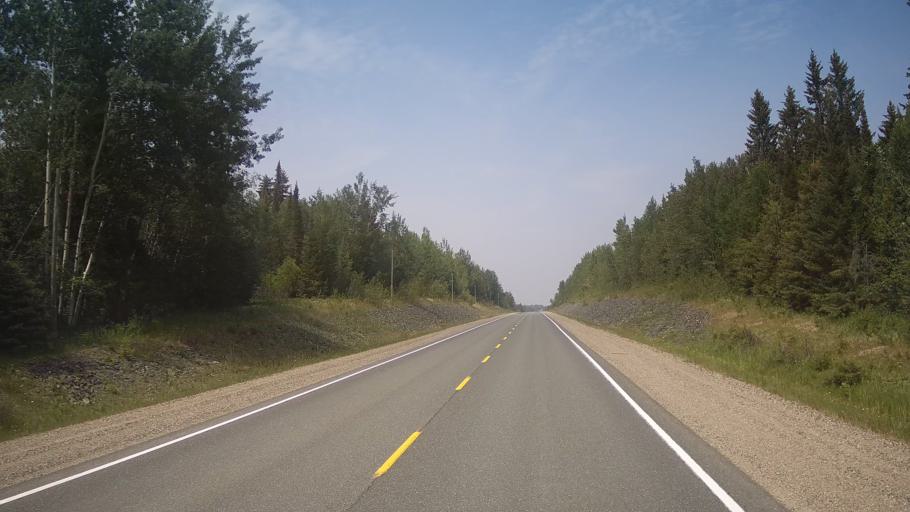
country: CA
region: Ontario
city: Timmins
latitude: 48.7481
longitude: -81.3579
